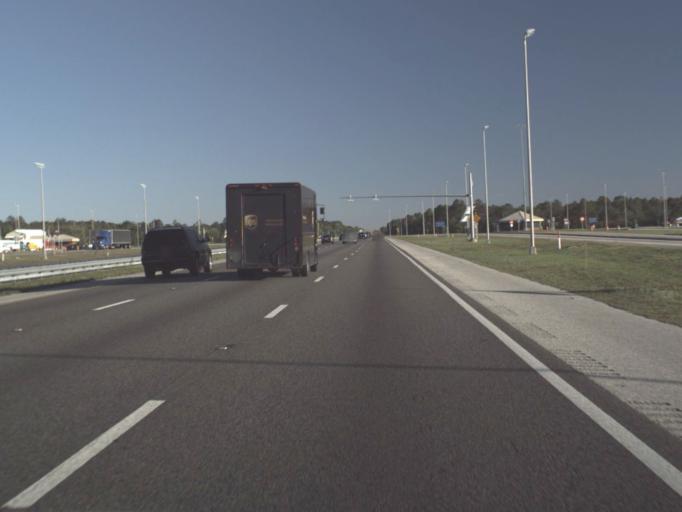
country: US
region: Florida
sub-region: Flagler County
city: Palm Coast
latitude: 29.5127
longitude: -81.1980
